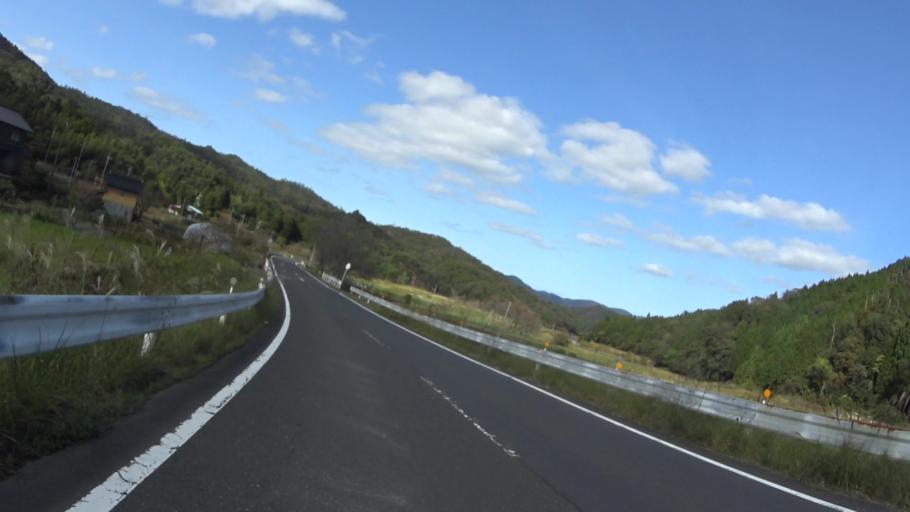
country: JP
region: Hyogo
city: Toyooka
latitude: 35.5478
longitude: 134.9784
